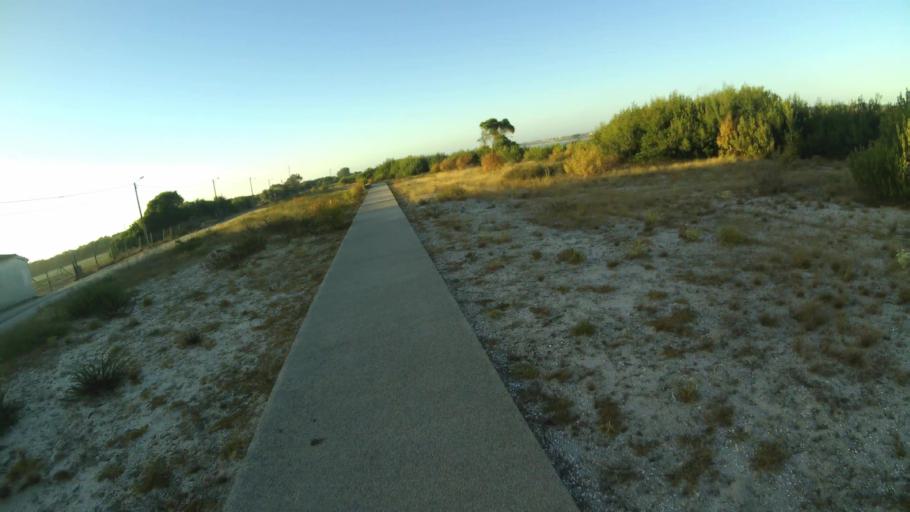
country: PT
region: Aveiro
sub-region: Ilhavo
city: Gafanha da Encarnacao
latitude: 40.5711
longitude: -8.7563
